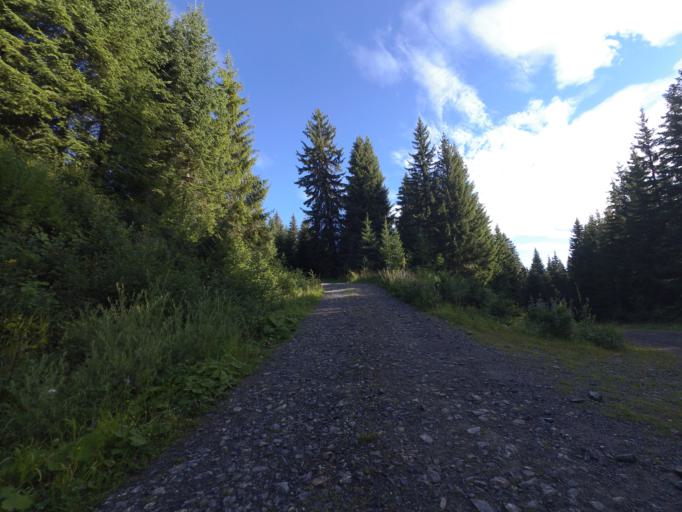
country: AT
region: Salzburg
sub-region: Politischer Bezirk Sankt Johann im Pongau
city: Goldegg
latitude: 47.3526
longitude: 13.0949
